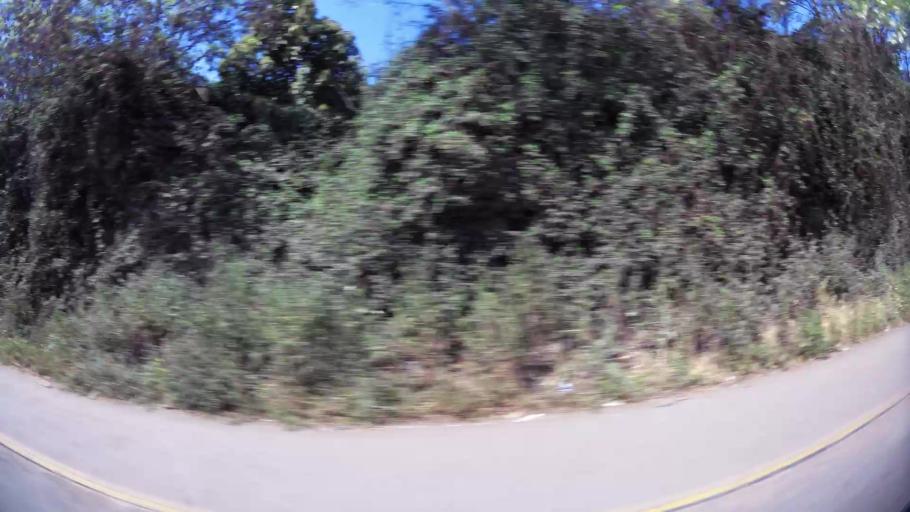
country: CL
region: Santiago Metropolitan
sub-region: Provincia de Talagante
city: Talagante
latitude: -33.6483
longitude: -70.9186
